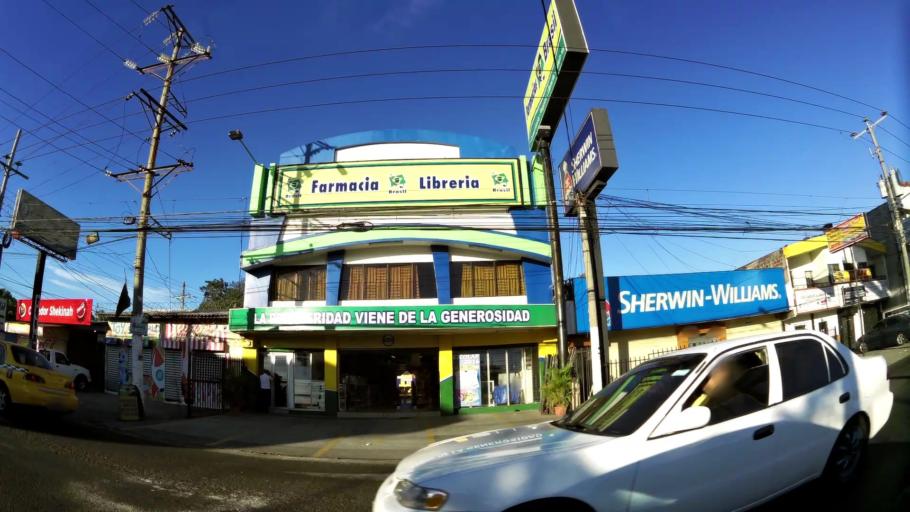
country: SV
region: San Miguel
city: San Miguel
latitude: 13.4858
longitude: -88.1857
